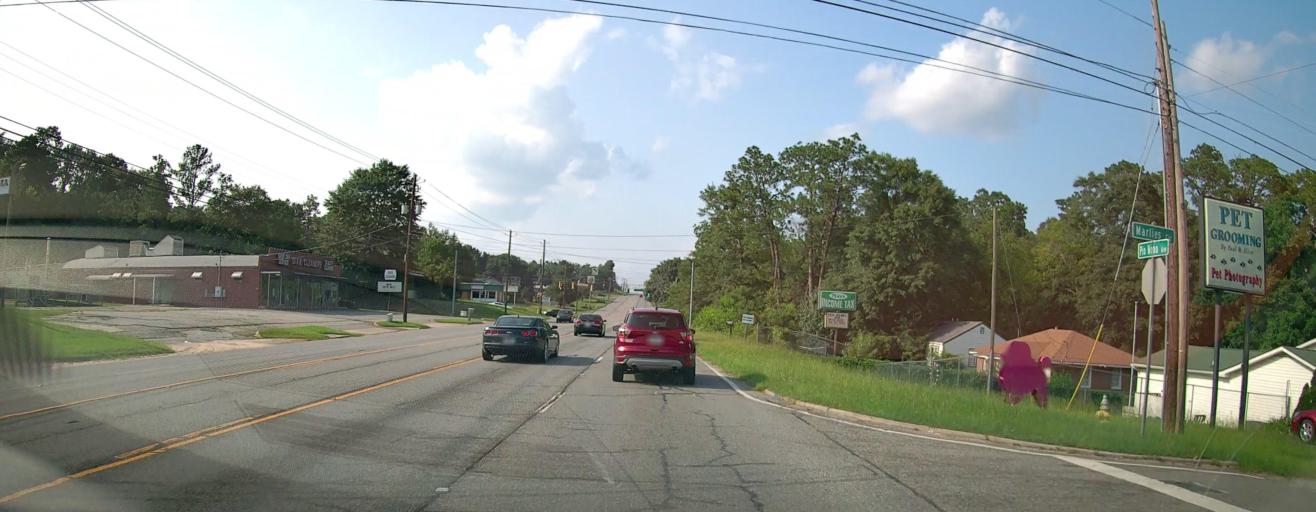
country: US
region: Georgia
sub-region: Bibb County
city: Macon
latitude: 32.8048
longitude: -83.6630
